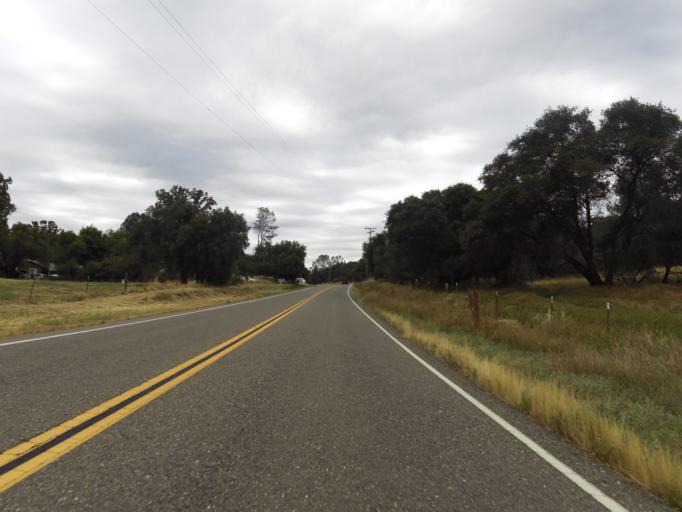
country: US
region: California
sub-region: Madera County
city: Coarsegold
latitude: 37.2478
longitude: -119.7288
